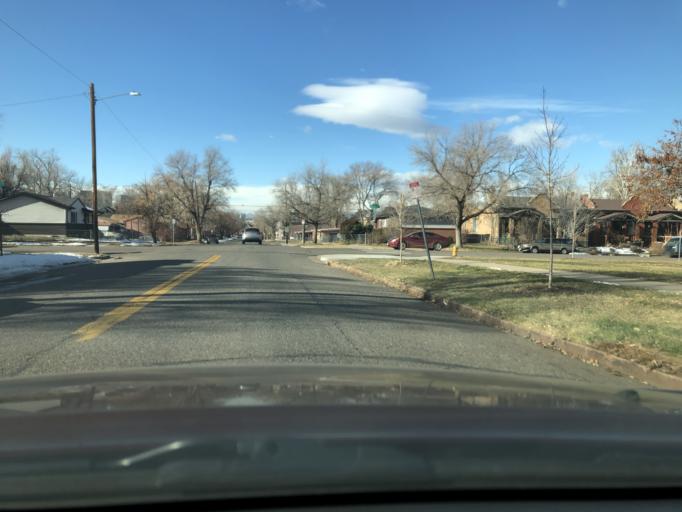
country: US
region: Colorado
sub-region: Denver County
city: Denver
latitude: 39.7545
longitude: -104.9691
